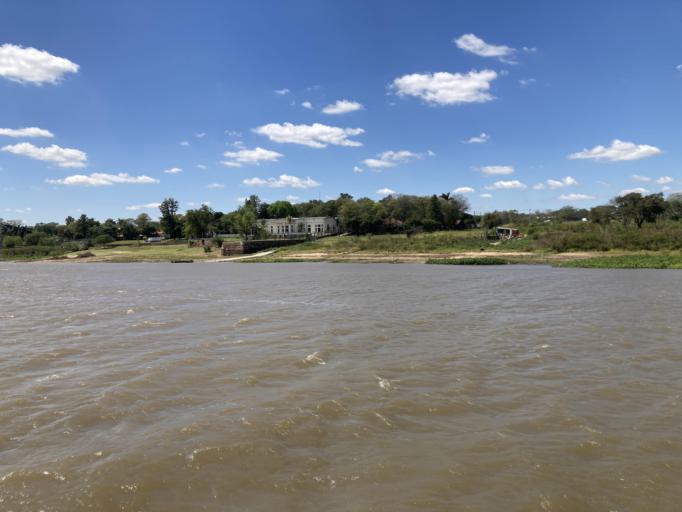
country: PY
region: Central
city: Colonia Mariano Roque Alonso
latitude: -25.1945
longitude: -57.5559
